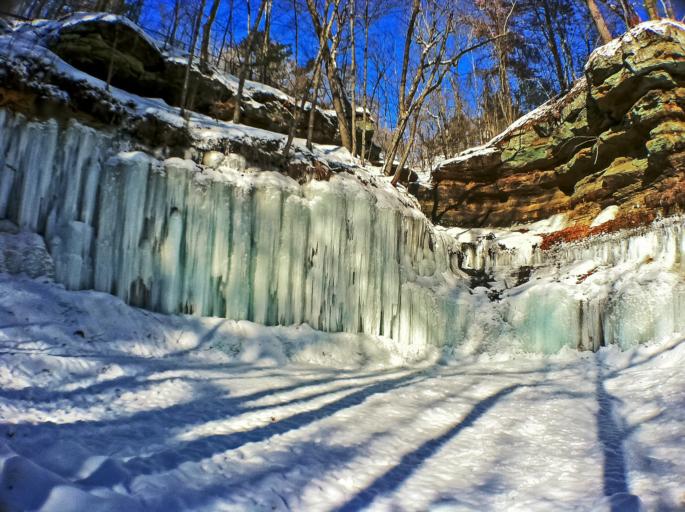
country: US
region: Wisconsin
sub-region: Dunn County
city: Menomonie
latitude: 44.8503
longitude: -91.9523
